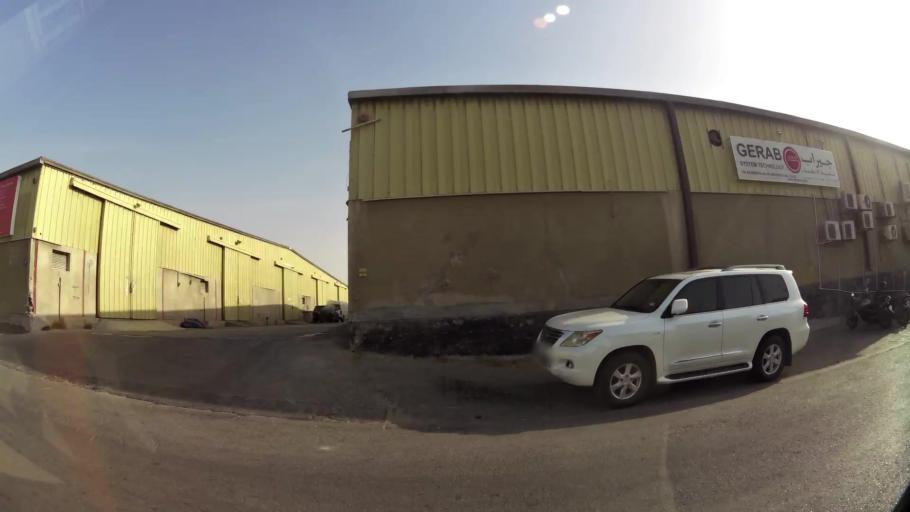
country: AE
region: Ash Shariqah
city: Sharjah
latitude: 25.2316
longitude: 55.3740
